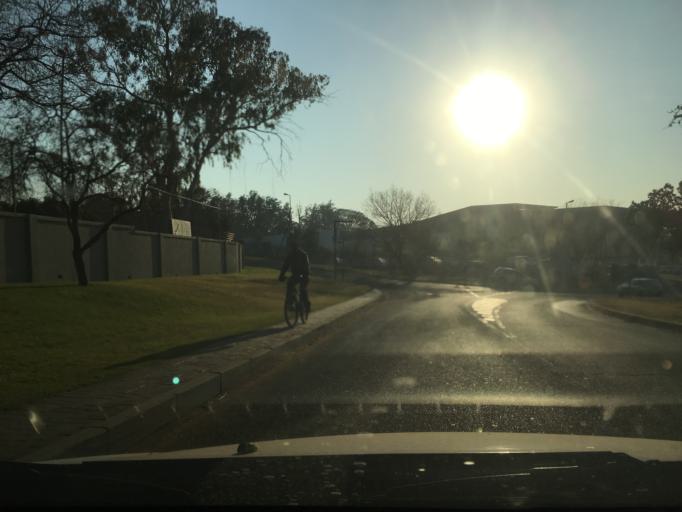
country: ZA
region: Gauteng
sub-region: City of Johannesburg Metropolitan Municipality
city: Johannesburg
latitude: -26.0756
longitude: 28.0247
